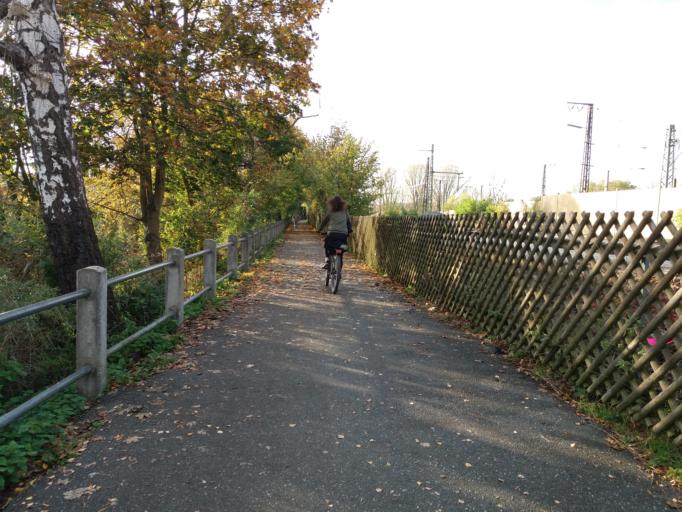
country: DE
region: Bavaria
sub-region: Regierungsbezirk Mittelfranken
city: Furth
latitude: 49.4706
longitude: 10.9845
